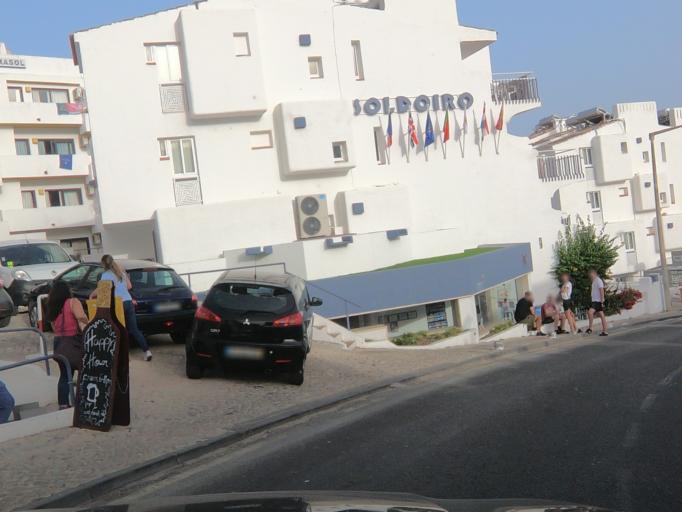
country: PT
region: Faro
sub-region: Albufeira
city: Albufeira
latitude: 37.0881
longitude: -8.2261
